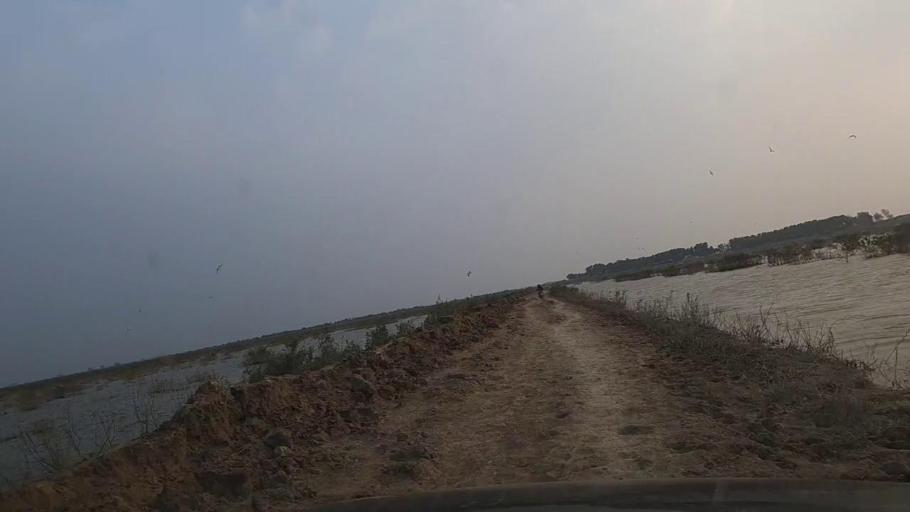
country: PK
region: Sindh
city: Gharo
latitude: 24.7678
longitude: 67.6917
